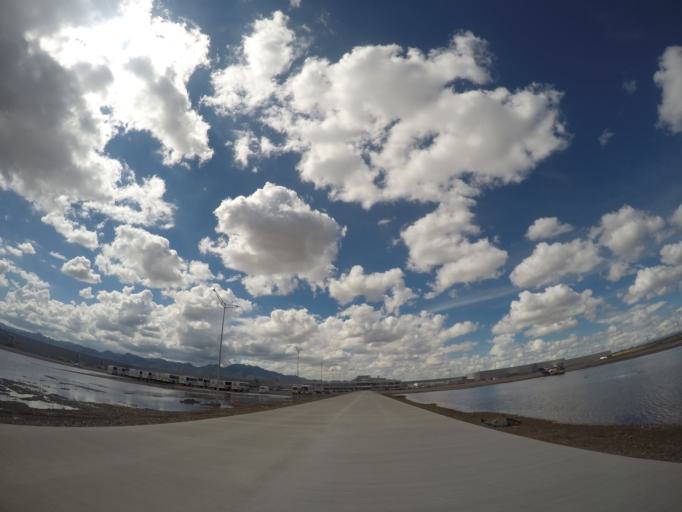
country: MX
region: San Luis Potosi
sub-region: Zaragoza
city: Cerro Gordo
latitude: 21.9654
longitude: -100.8451
